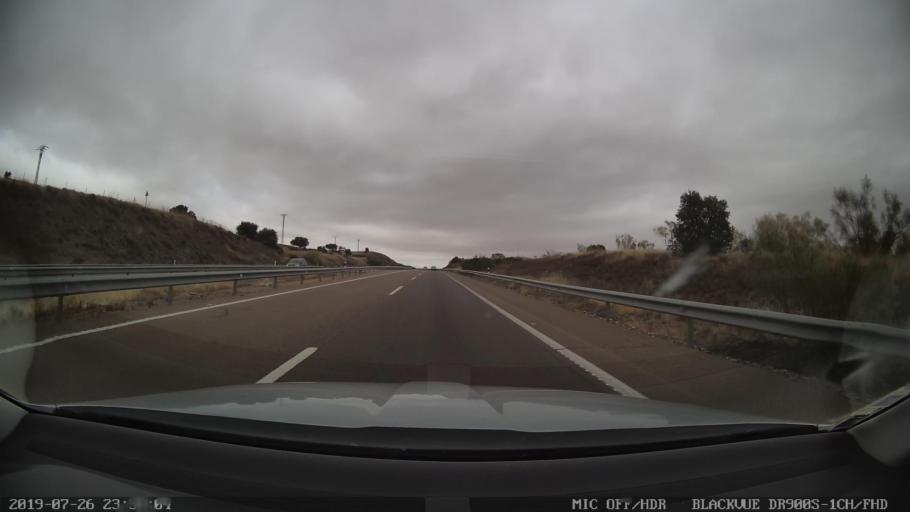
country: ES
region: Extremadura
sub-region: Provincia de Caceres
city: Santa Cruz de la Sierra
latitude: 39.3531
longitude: -5.8606
